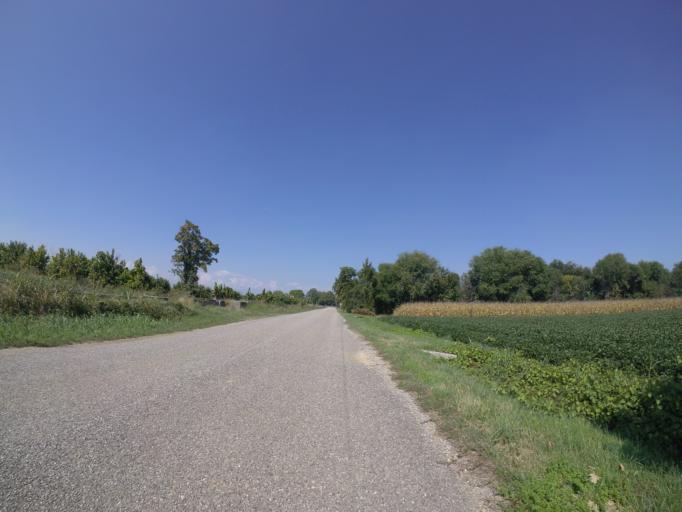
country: IT
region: Friuli Venezia Giulia
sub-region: Provincia di Udine
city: Bertiolo
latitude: 45.9423
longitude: 13.0890
